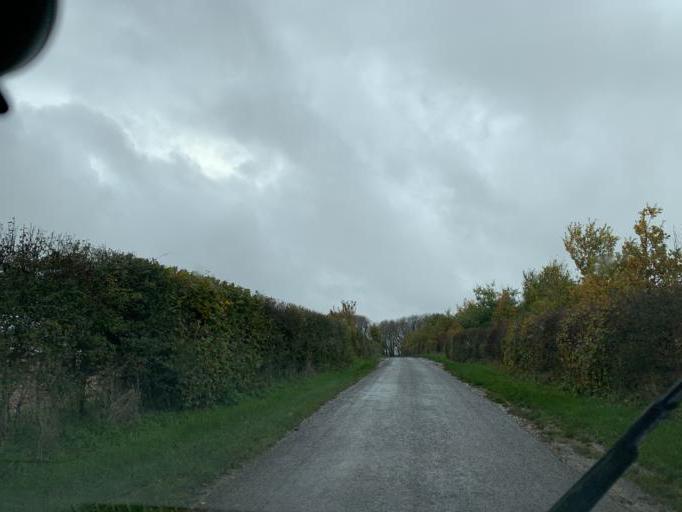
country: GB
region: England
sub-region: Wiltshire
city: Amesbury
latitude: 51.1534
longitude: -1.7814
